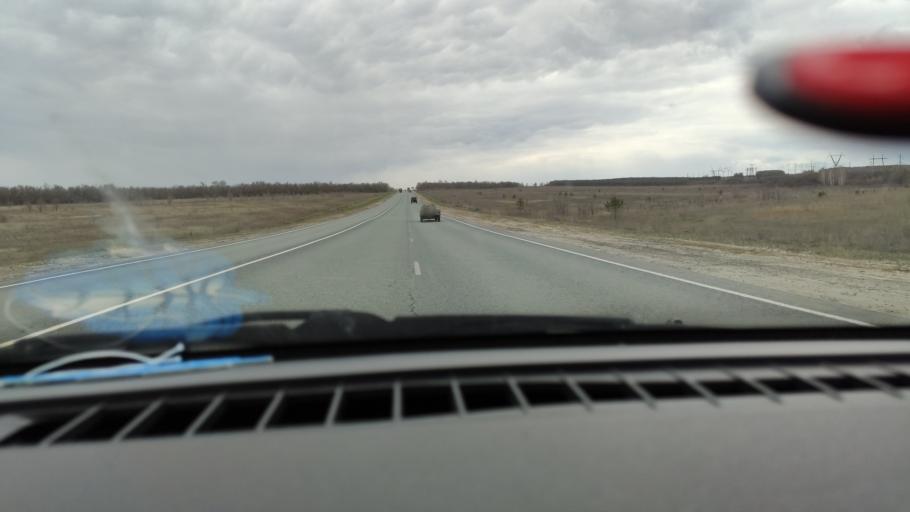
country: RU
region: Saratov
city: Sinodskoye
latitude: 51.9117
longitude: 46.5539
